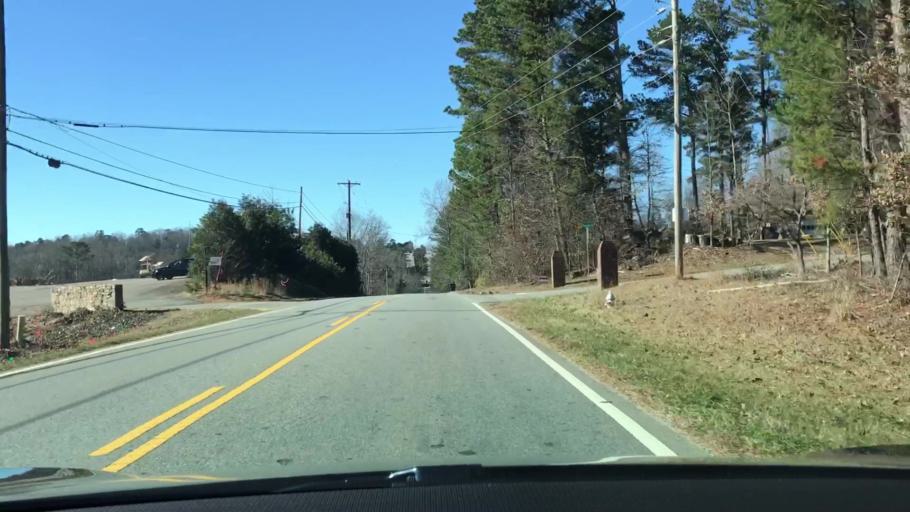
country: US
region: Georgia
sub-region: Forsyth County
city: Cumming
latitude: 34.1822
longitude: -84.0964
